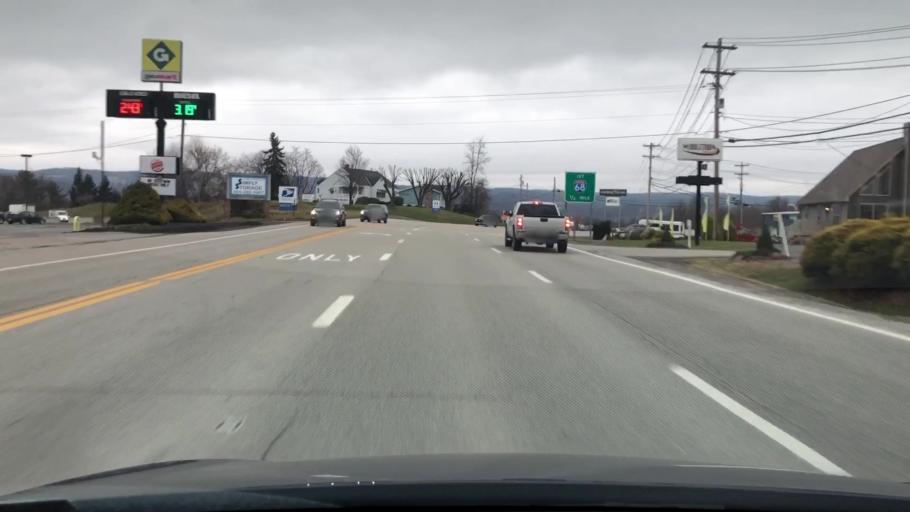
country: US
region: West Virginia
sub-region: Monongalia County
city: Morgantown
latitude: 39.5943
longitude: -79.9549
